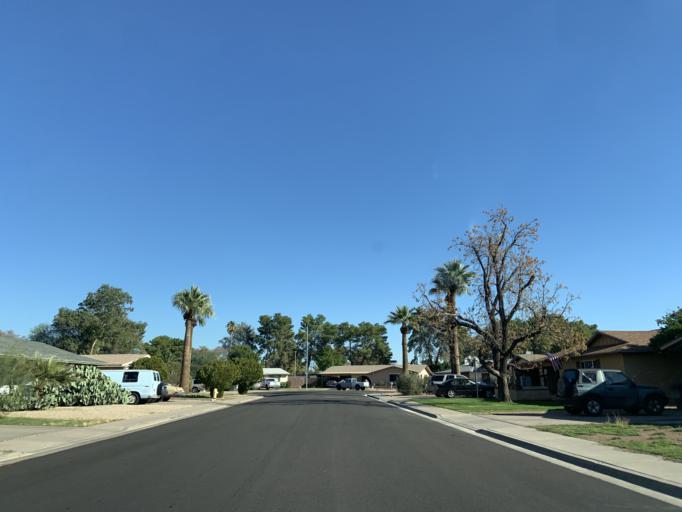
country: US
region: Arizona
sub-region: Maricopa County
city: Tempe
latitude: 33.4018
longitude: -111.8776
